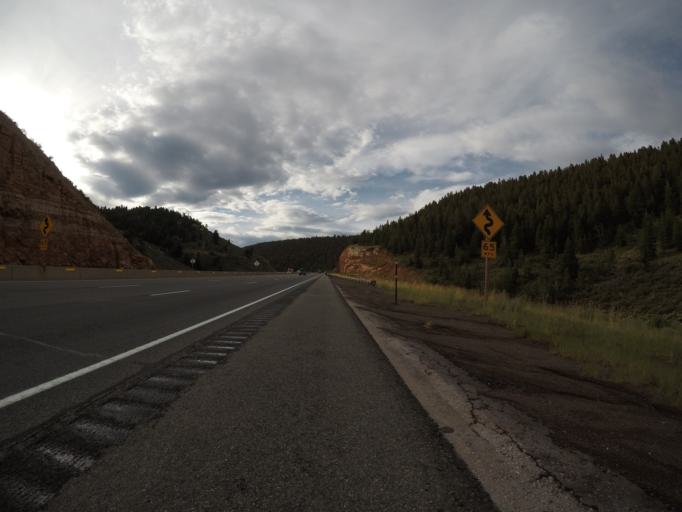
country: US
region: Wyoming
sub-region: Albany County
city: Laramie
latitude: 41.2692
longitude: -105.4793
